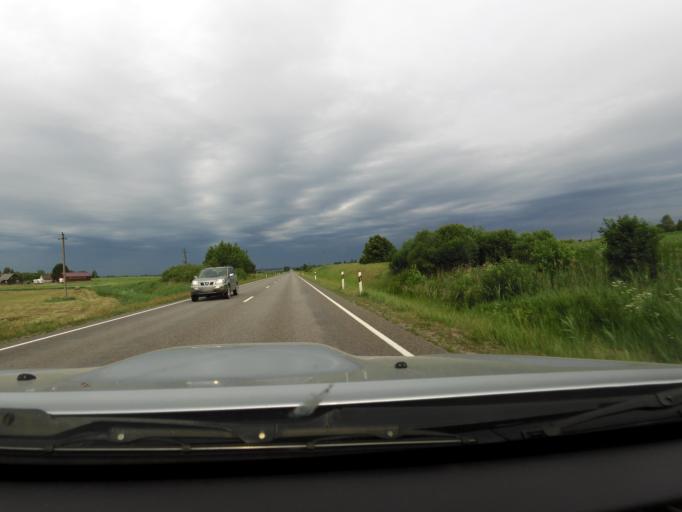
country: LT
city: Aukstadvaris
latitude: 54.5760
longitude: 24.3496
